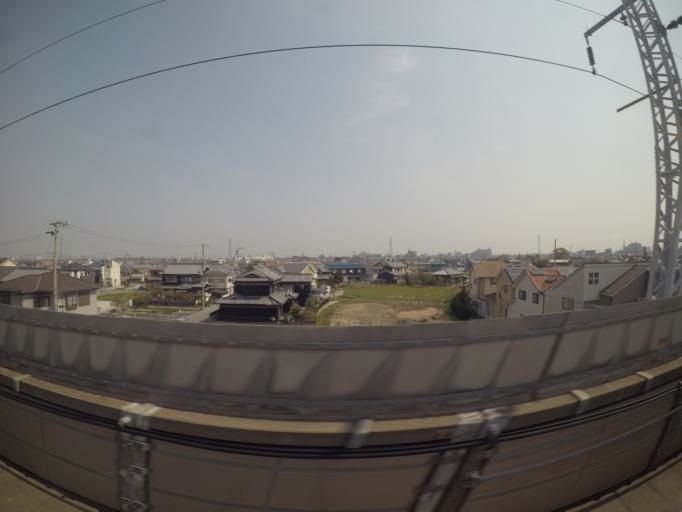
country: JP
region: Hyogo
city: Kakogawacho-honmachi
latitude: 34.7135
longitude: 134.8758
